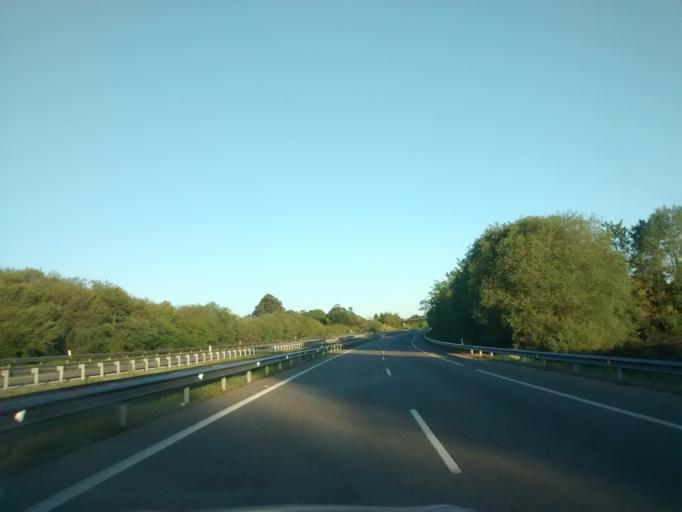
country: ES
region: Asturias
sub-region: Province of Asturias
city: Carrena
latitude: 43.4437
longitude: -4.9094
